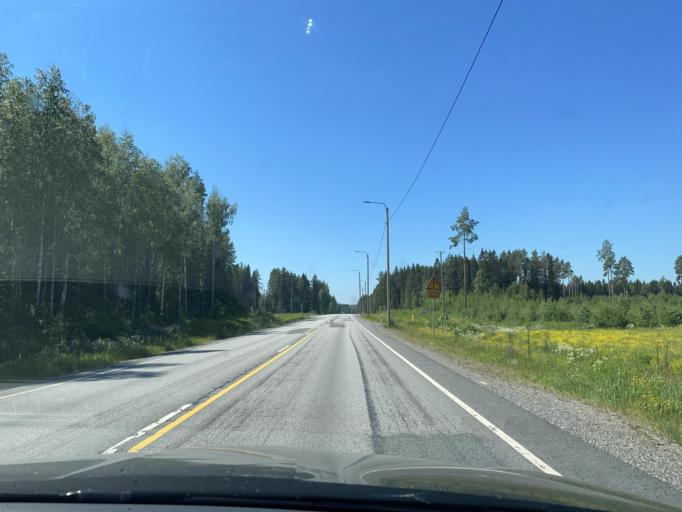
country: FI
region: Central Finland
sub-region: Saarijaervi-Viitasaari
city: Viitasaari
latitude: 63.1739
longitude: 26.0167
